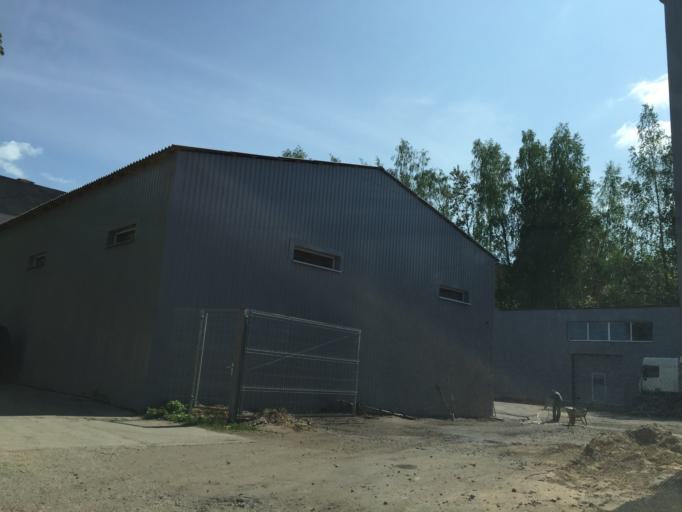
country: LV
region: Riga
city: Bergi
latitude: 56.9991
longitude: 24.2665
